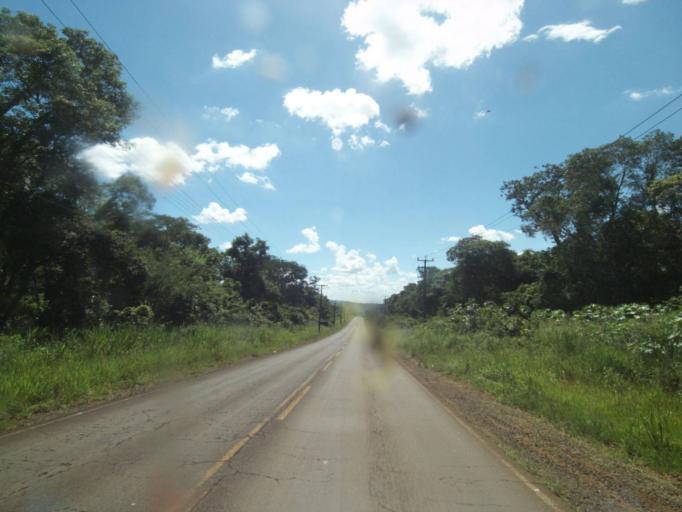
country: BR
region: Parana
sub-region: Chopinzinho
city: Chopinzinho
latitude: -25.7794
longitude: -52.1028
